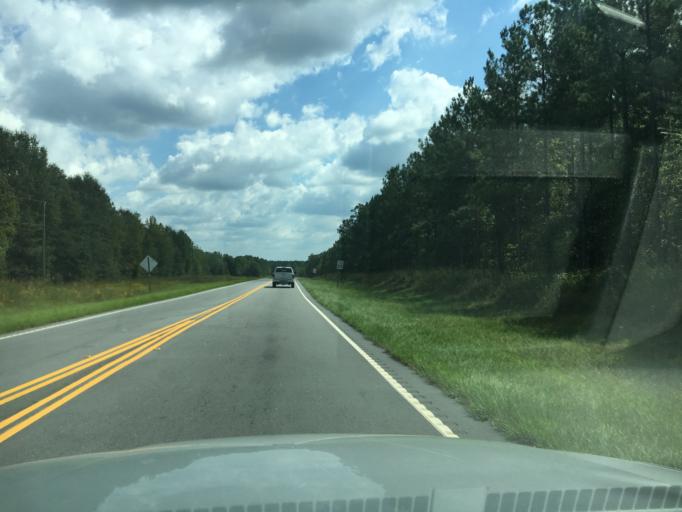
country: US
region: South Carolina
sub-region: Greenwood County
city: Greenwood
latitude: 34.1414
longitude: -82.1471
